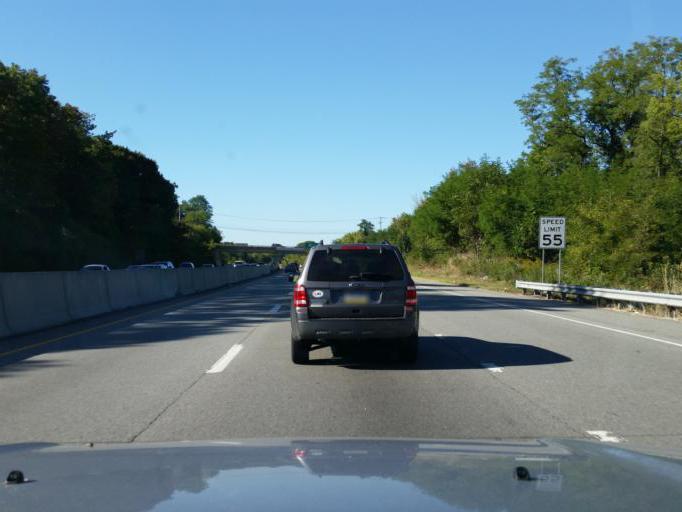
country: US
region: Pennsylvania
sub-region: Chester County
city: West Chester
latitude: 39.9758
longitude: -75.5849
